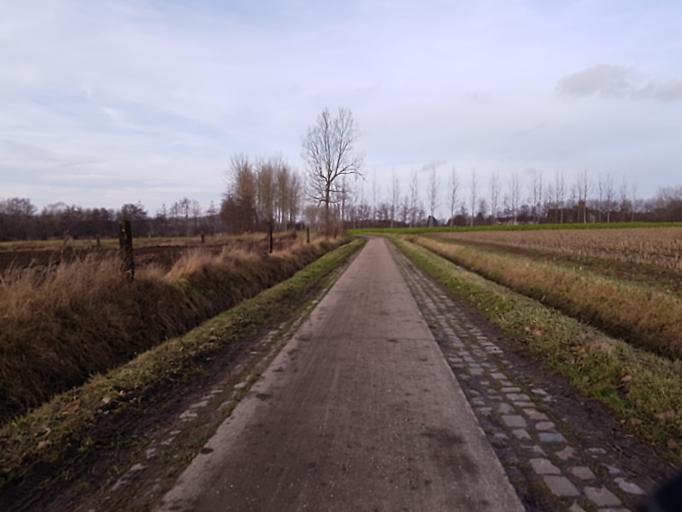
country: BE
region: Flanders
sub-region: Provincie Vlaams-Brabant
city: Rotselaar
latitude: 50.9438
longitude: 4.7017
